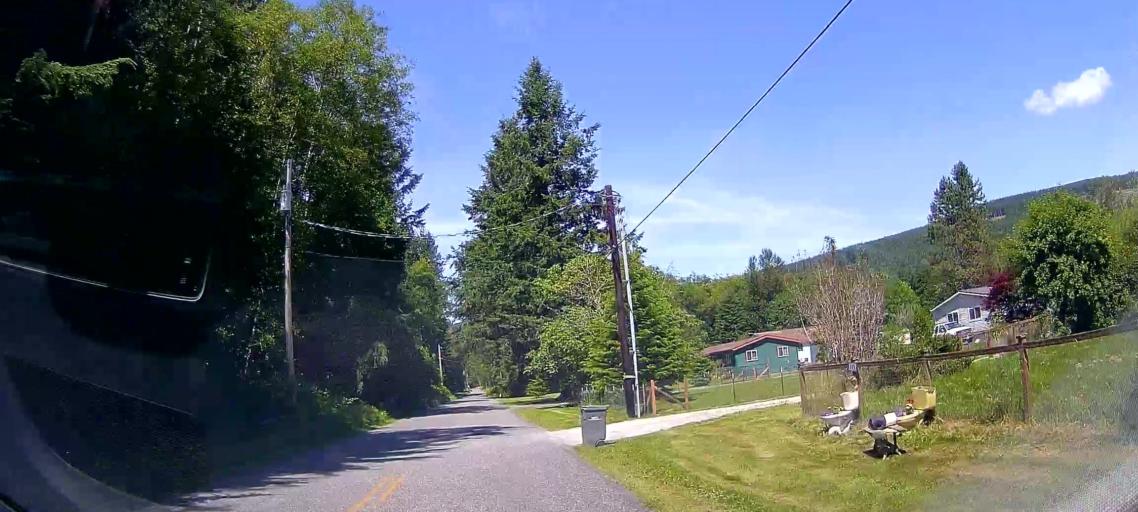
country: US
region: Washington
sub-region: Skagit County
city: Burlington
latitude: 48.5971
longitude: -122.3173
